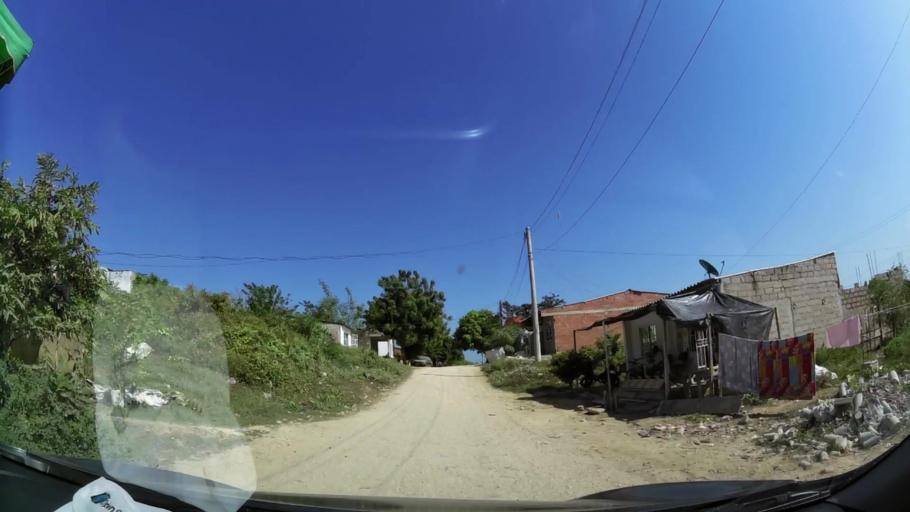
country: CO
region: Bolivar
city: Cartagena
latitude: 10.3654
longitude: -75.4989
